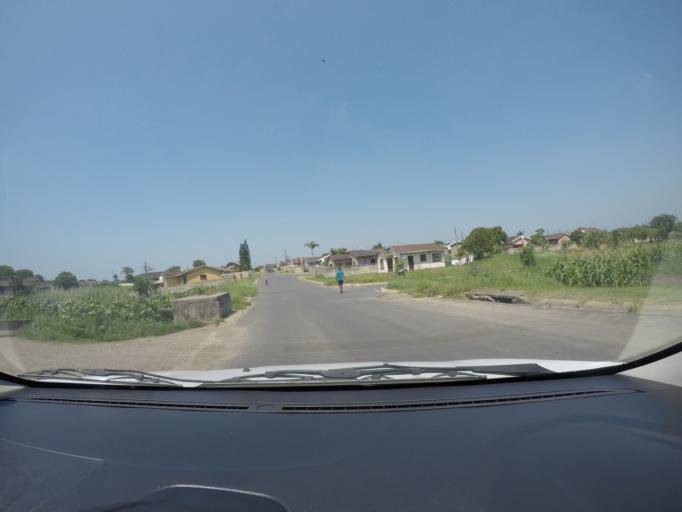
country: ZA
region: KwaZulu-Natal
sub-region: uThungulu District Municipality
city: eSikhawini
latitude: -28.8654
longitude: 31.9212
